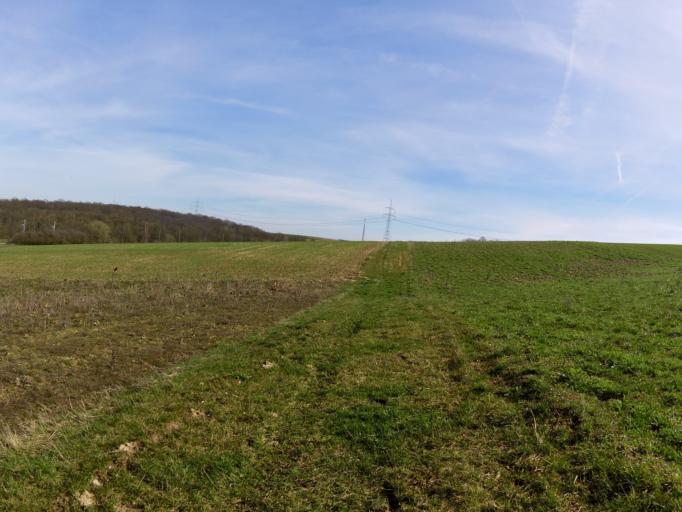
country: DE
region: Bavaria
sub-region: Regierungsbezirk Unterfranken
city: Rottendorf
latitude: 49.8056
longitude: 10.0607
